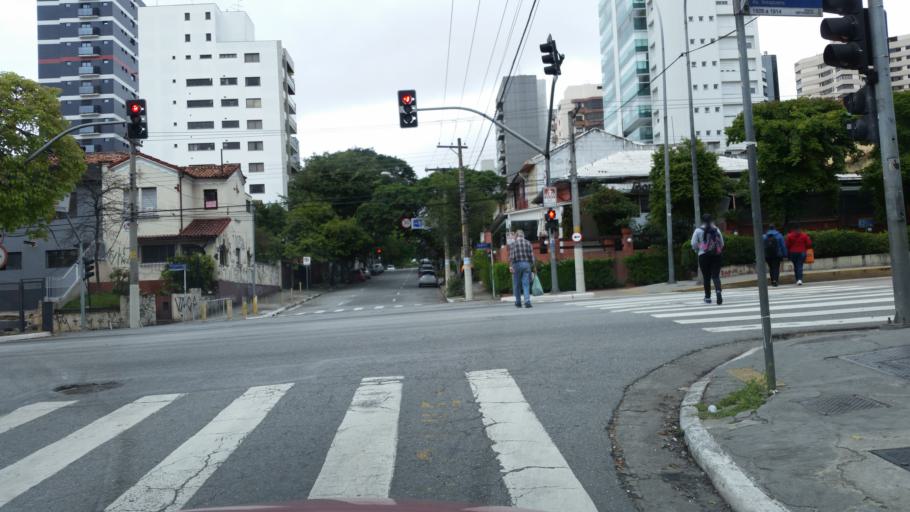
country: BR
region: Sao Paulo
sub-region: Sao Paulo
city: Sao Paulo
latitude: -23.6008
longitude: -46.6599
